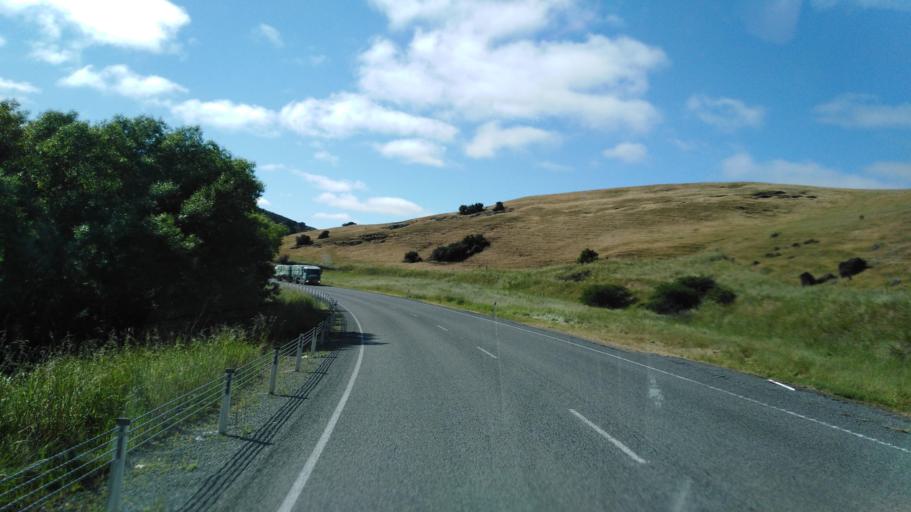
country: NZ
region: Canterbury
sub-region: Hurunui District
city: Amberley
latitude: -43.0174
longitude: 172.7041
